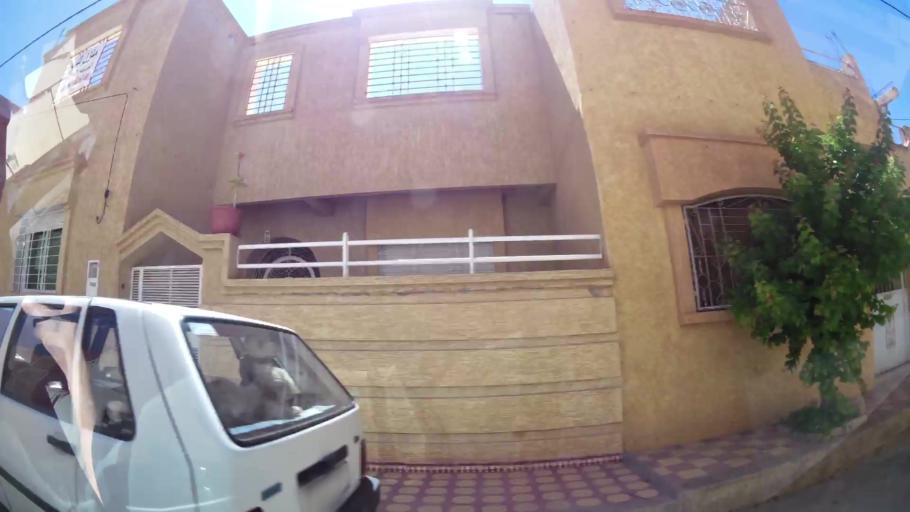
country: MA
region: Oriental
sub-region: Oujda-Angad
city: Oujda
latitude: 34.6681
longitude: -1.8691
